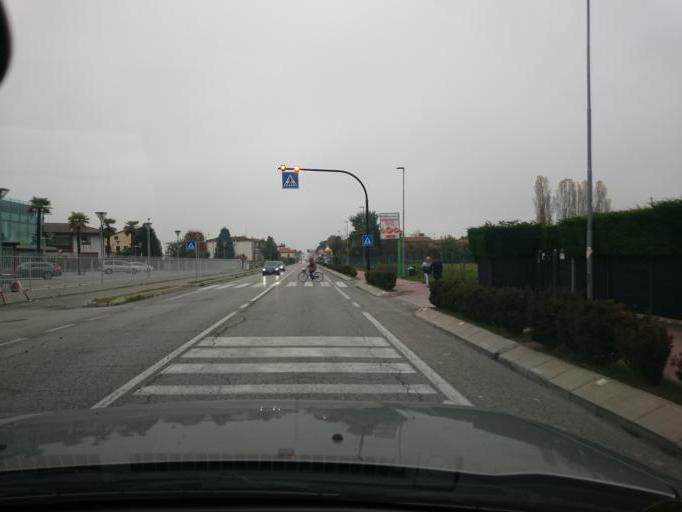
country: IT
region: Veneto
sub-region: Provincia di Padova
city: Legnaro
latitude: 45.3421
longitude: 11.9692
